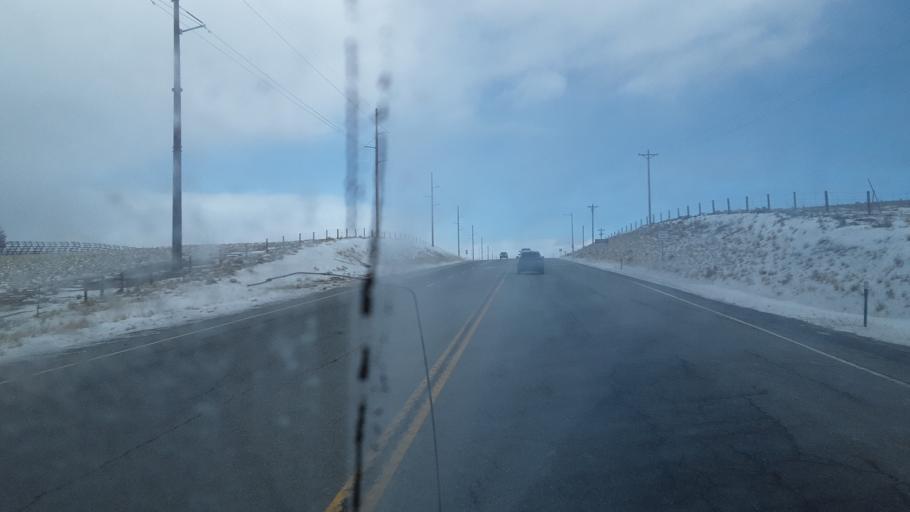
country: US
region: Colorado
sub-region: Park County
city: Fairplay
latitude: 39.3138
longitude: -105.8835
